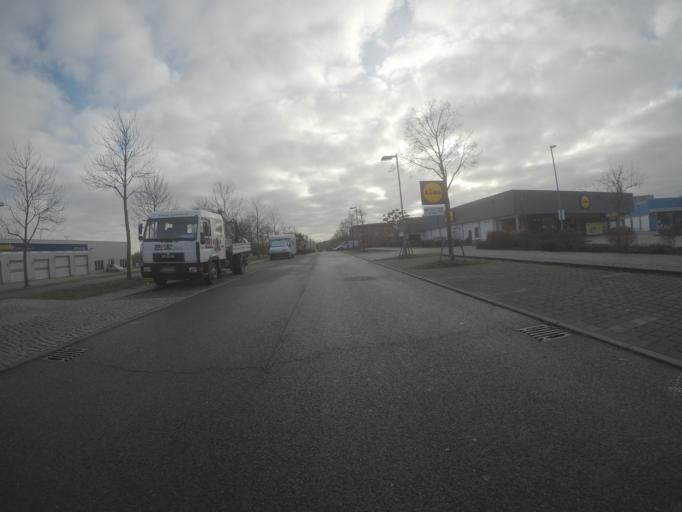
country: DE
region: Berlin
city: Marzahn
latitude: 52.5462
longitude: 13.5758
